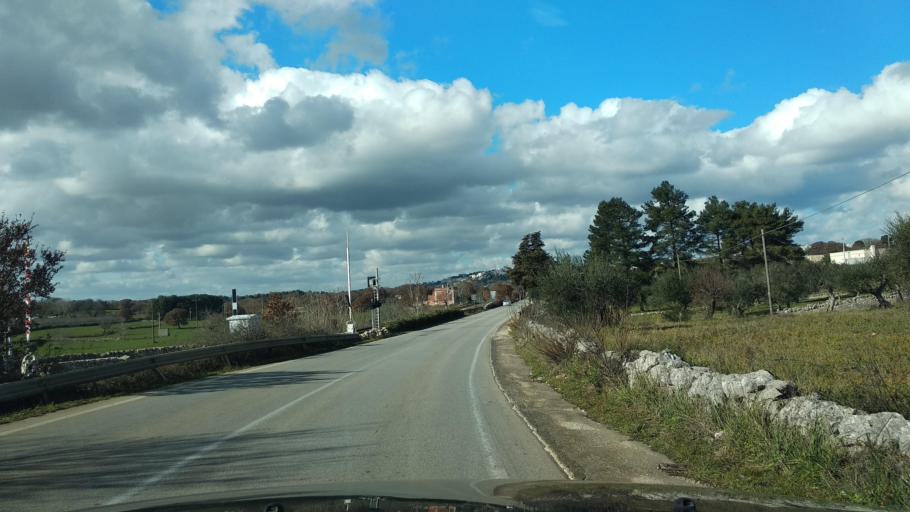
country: IT
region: Apulia
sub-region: Provincia di Brindisi
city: Cisternino
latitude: 40.7235
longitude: 17.4452
